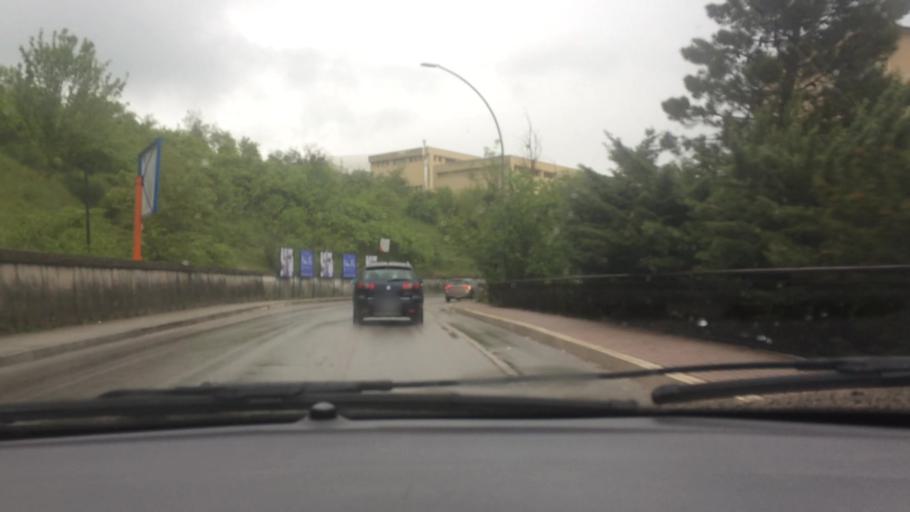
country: IT
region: Basilicate
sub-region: Provincia di Potenza
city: Potenza
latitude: 40.6431
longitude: 15.7961
